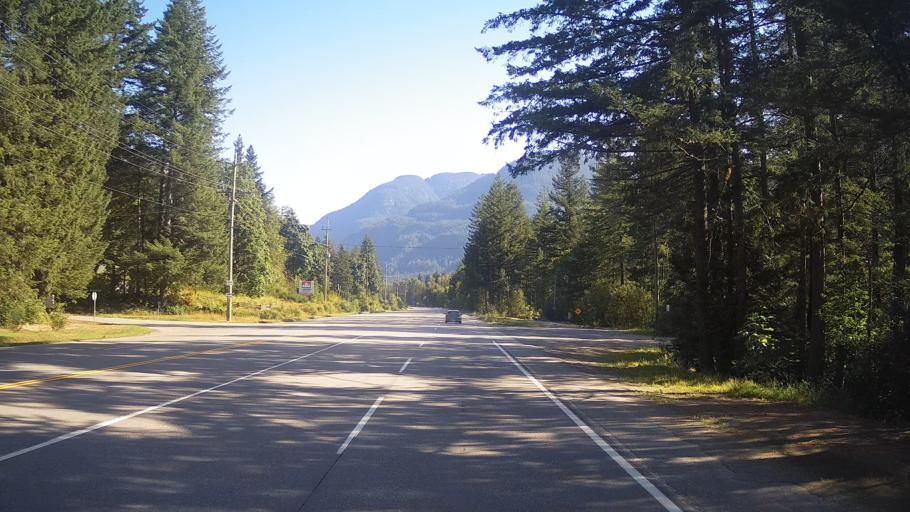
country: CA
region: British Columbia
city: Hope
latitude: 49.4750
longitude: -121.4260
